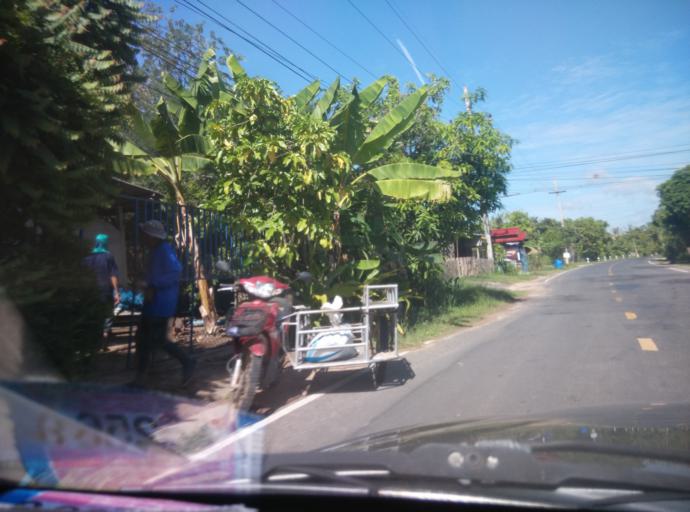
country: TH
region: Sisaket
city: Uthumphon Phisai
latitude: 15.1195
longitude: 104.2247
